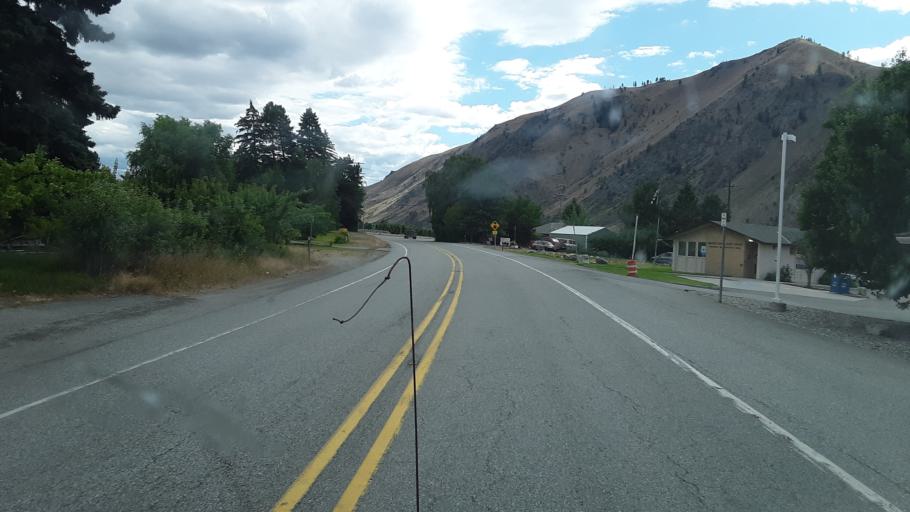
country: US
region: Washington
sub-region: Chelan County
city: Entiat
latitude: 47.6255
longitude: -120.2266
